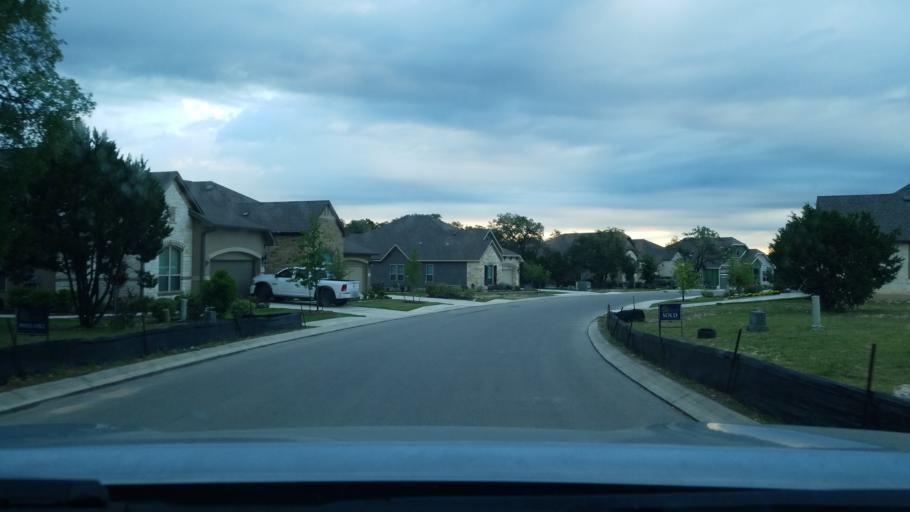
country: US
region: Texas
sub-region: Bexar County
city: Timberwood Park
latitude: 29.7157
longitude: -98.4582
